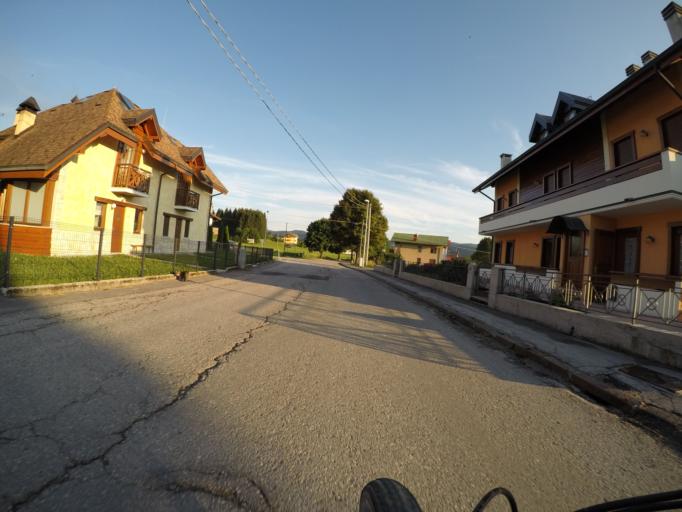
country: IT
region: Veneto
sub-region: Provincia di Vicenza
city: Asiago
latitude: 45.8838
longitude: 11.5195
